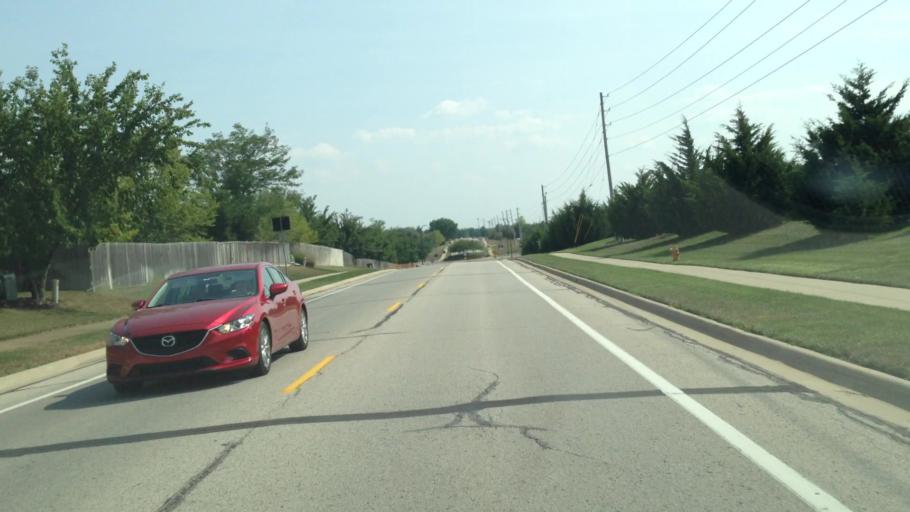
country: US
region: Kansas
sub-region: Douglas County
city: Lawrence
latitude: 38.9667
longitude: -95.3257
